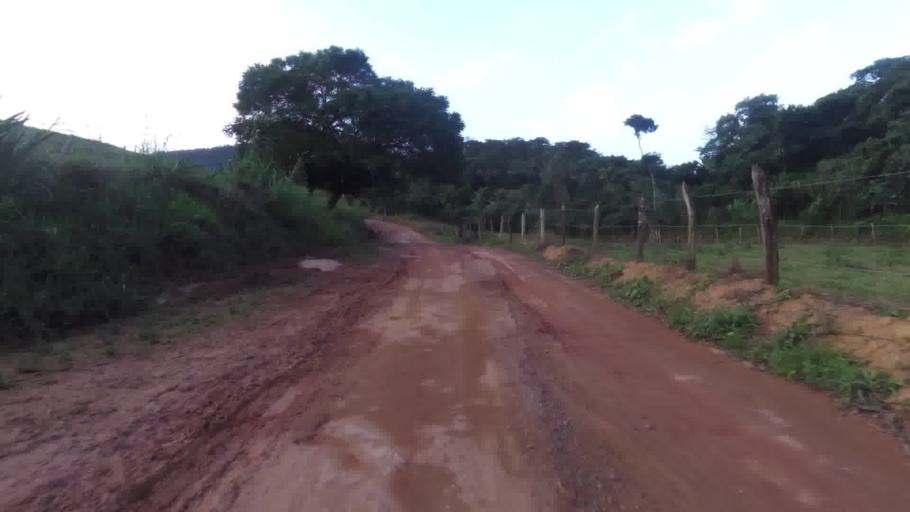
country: BR
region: Espirito Santo
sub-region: Guarapari
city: Guarapari
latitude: -20.6887
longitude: -40.6282
